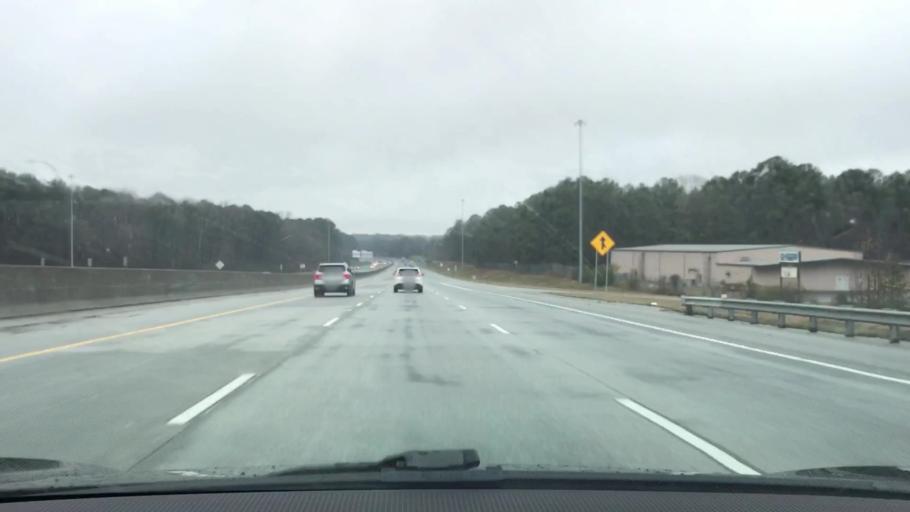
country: US
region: Georgia
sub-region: Newton County
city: Oxford
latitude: 33.6154
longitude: -83.8467
